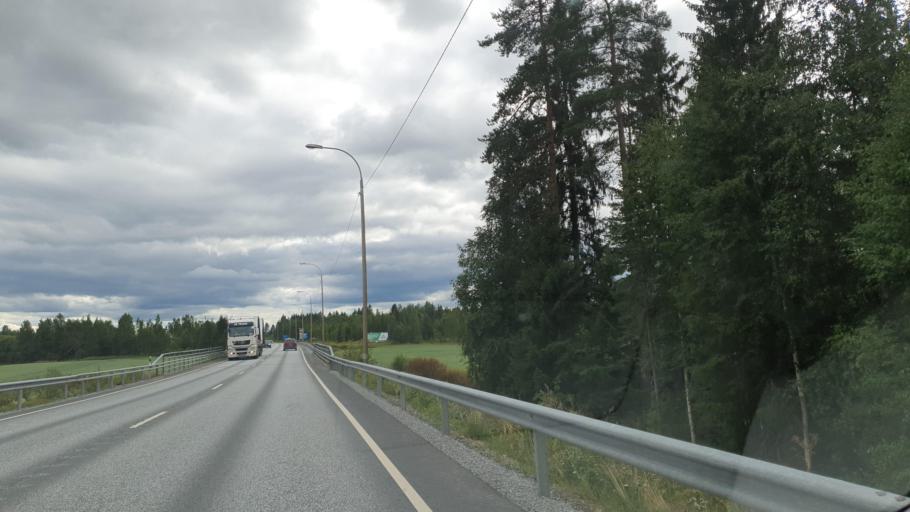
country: FI
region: Northern Savo
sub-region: Ylae-Savo
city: Sonkajaervi
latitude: 63.8766
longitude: 27.4407
